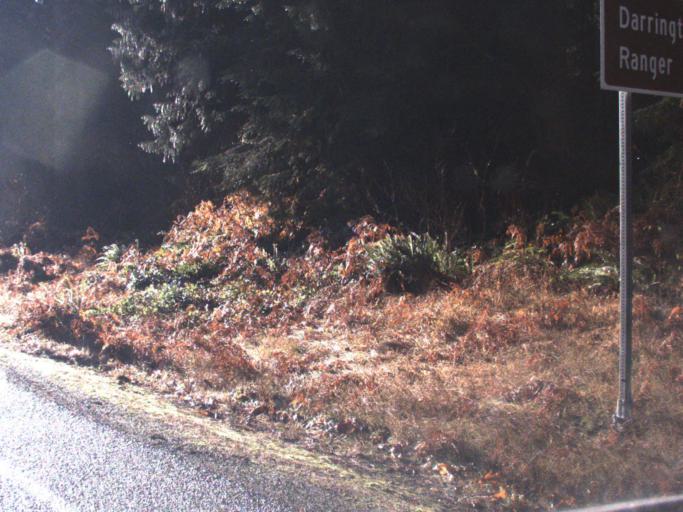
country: US
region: Washington
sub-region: Snohomish County
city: Darrington
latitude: 48.3648
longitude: -121.5398
